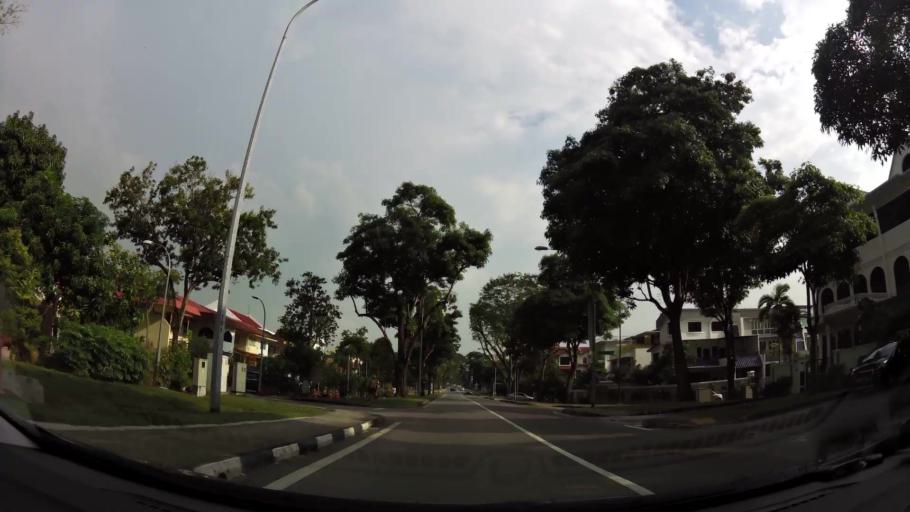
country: SG
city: Singapore
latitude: 1.3242
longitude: 103.9531
